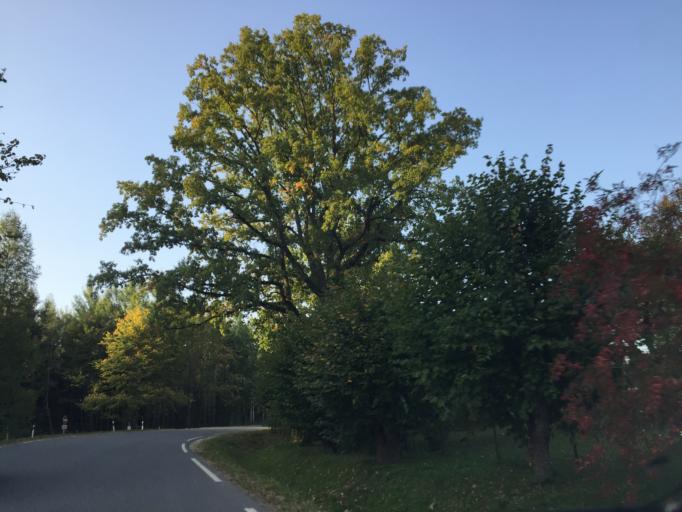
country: LV
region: Kegums
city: Kegums
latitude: 56.8147
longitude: 24.7480
